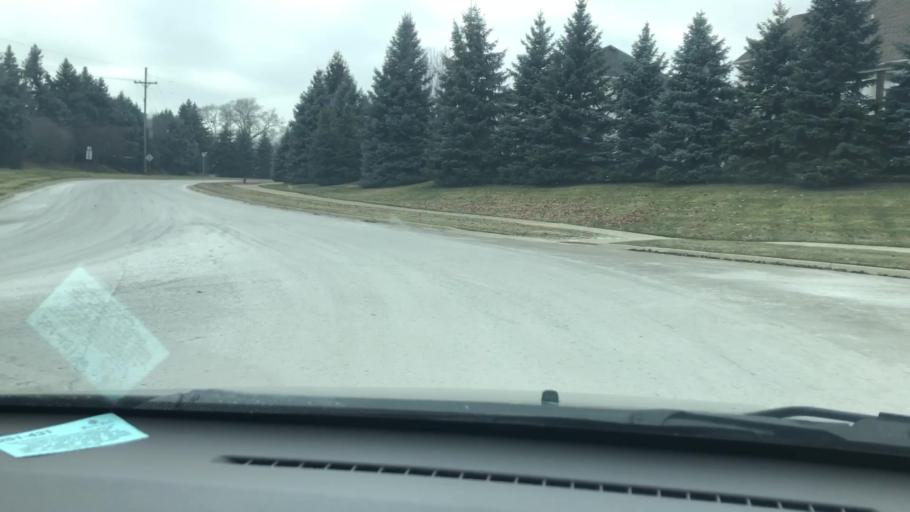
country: US
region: Michigan
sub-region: Oakland County
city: Rochester
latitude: 42.6936
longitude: -83.1175
